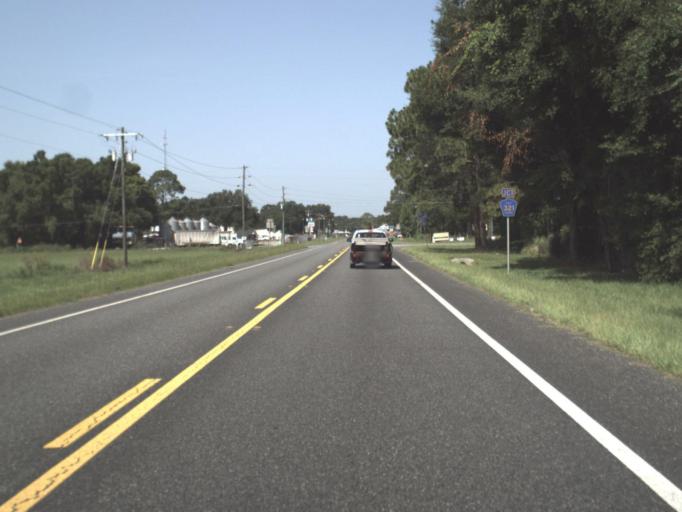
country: US
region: Florida
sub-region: Levy County
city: Chiefland
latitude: 29.4906
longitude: -82.8548
